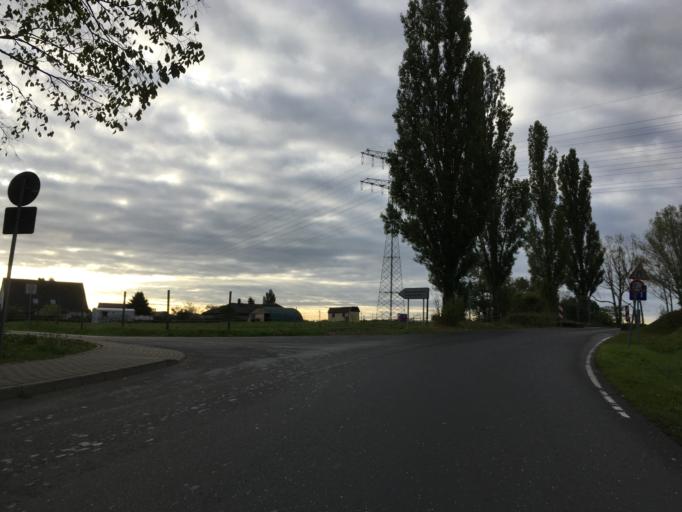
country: DE
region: Berlin
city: Wartenberg
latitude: 52.5930
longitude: 13.5271
